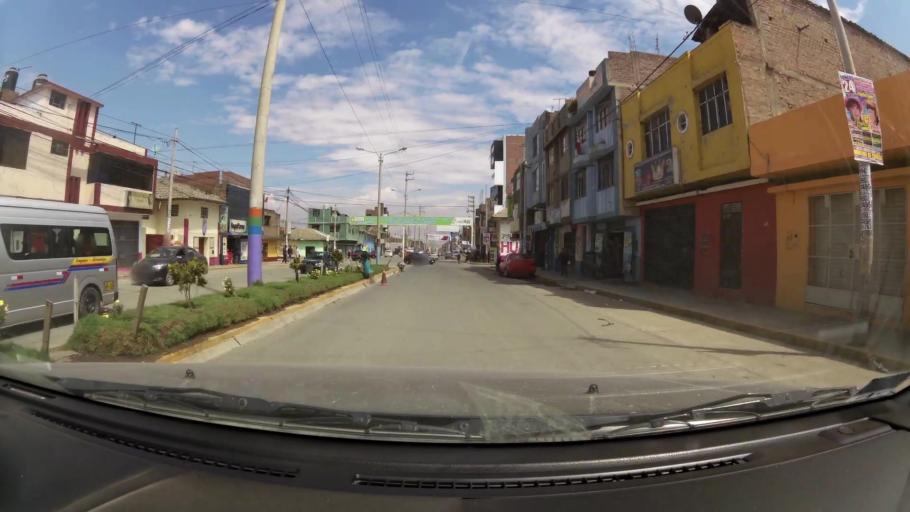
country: PE
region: Junin
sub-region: Provincia de Huancayo
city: Huancayo
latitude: -12.0834
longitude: -75.2038
